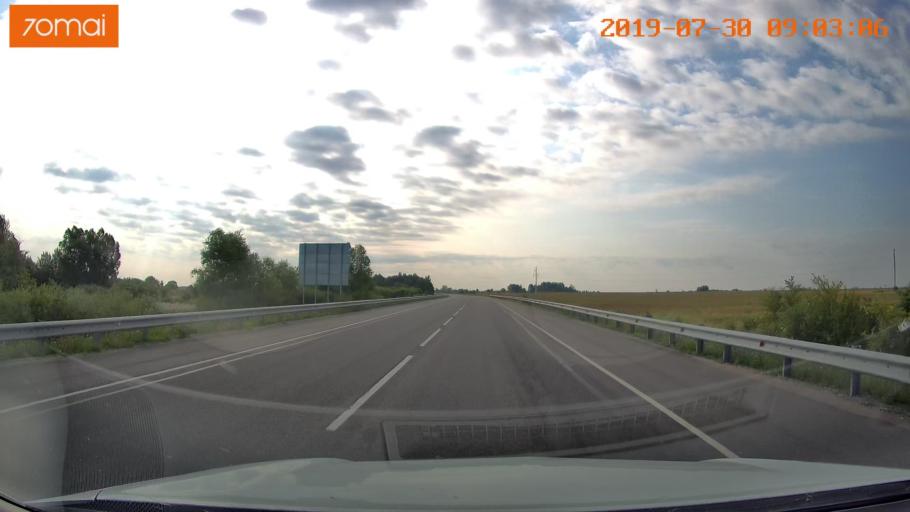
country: RU
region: Kaliningrad
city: Gusev
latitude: 54.6107
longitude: 22.2455
